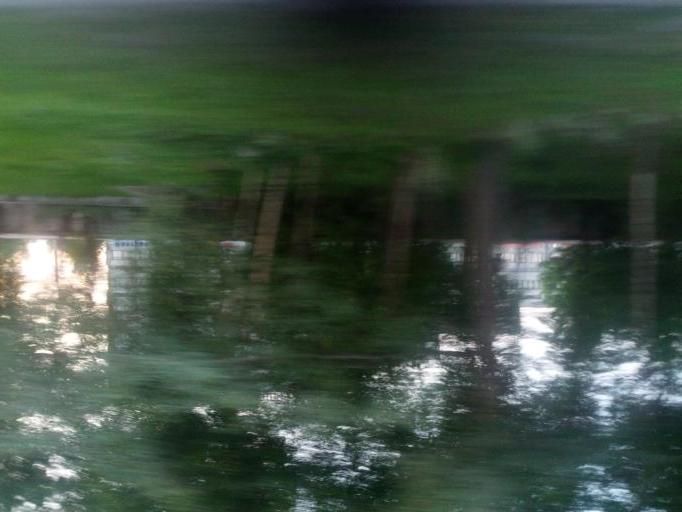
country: RU
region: St.-Petersburg
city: Staraya Derevnya
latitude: 59.9948
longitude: 30.2552
